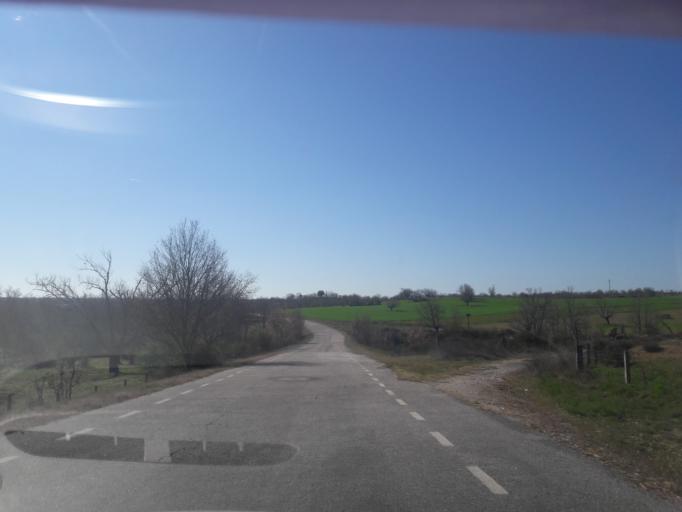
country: ES
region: Castille and Leon
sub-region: Provincia de Salamanca
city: Valsalabroso
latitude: 41.1621
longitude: -6.4966
